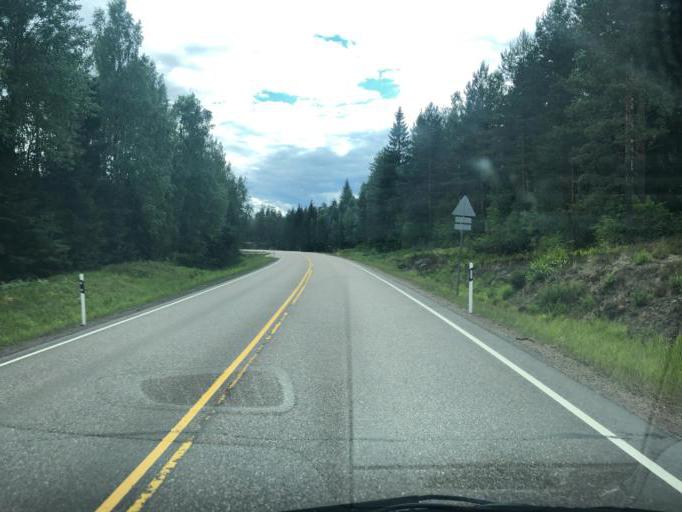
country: FI
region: Southern Savonia
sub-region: Mikkeli
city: Maentyharju
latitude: 61.1416
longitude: 27.1101
